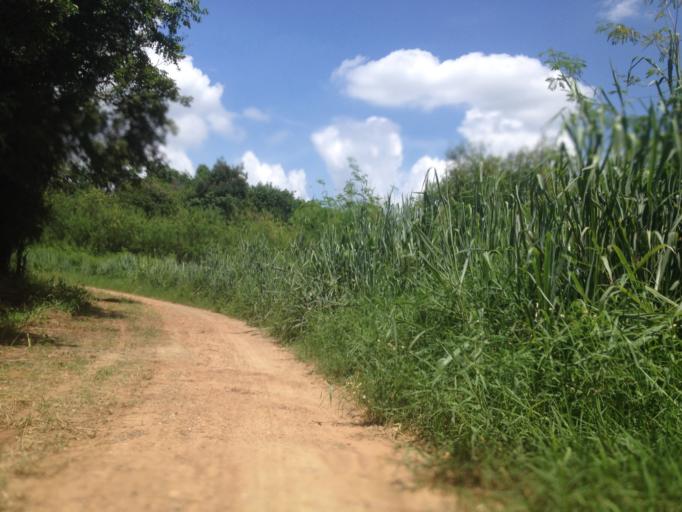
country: TH
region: Chiang Mai
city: Hang Dong
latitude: 18.7526
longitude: 98.9196
